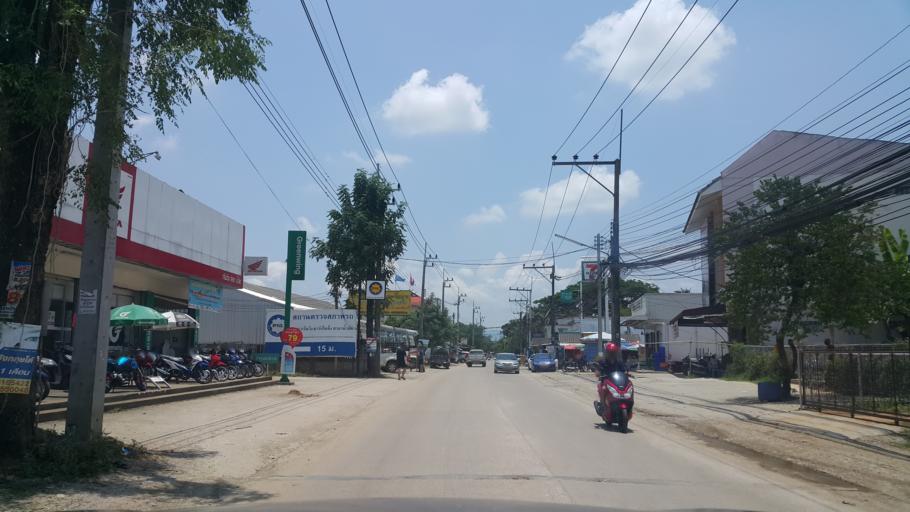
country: TH
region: Chiang Rai
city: Chiang Rai
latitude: 19.9288
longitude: 99.8158
